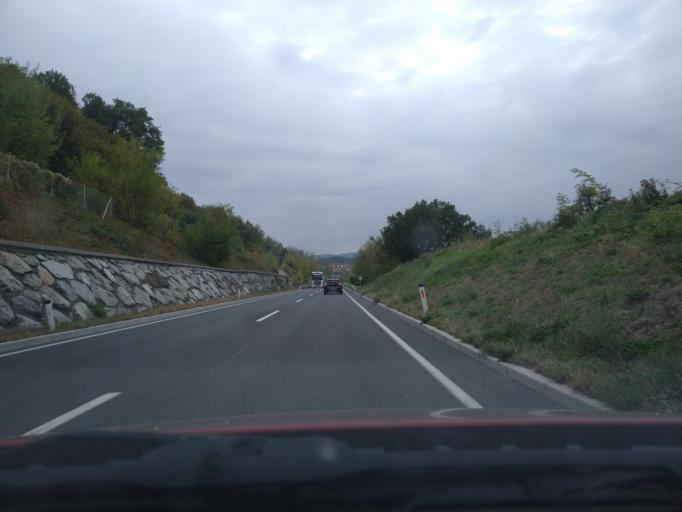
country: SI
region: Nova Gorica
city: Solkan
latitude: 45.9676
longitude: 13.6532
